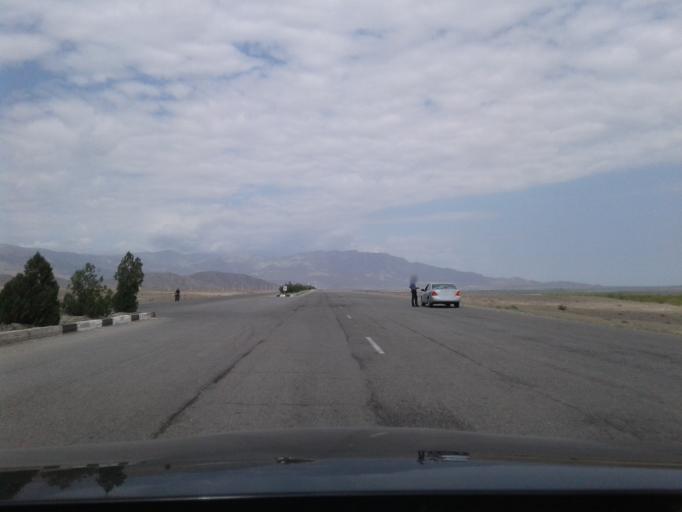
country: TM
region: Ahal
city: Baharly
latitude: 38.5084
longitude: 57.2696
